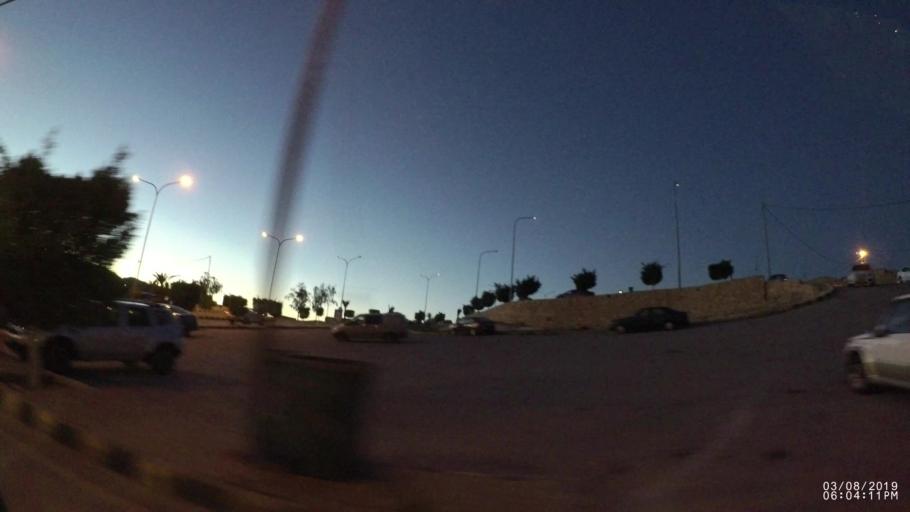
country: JO
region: Ma'an
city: Petra
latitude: 30.3259
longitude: 35.4685
